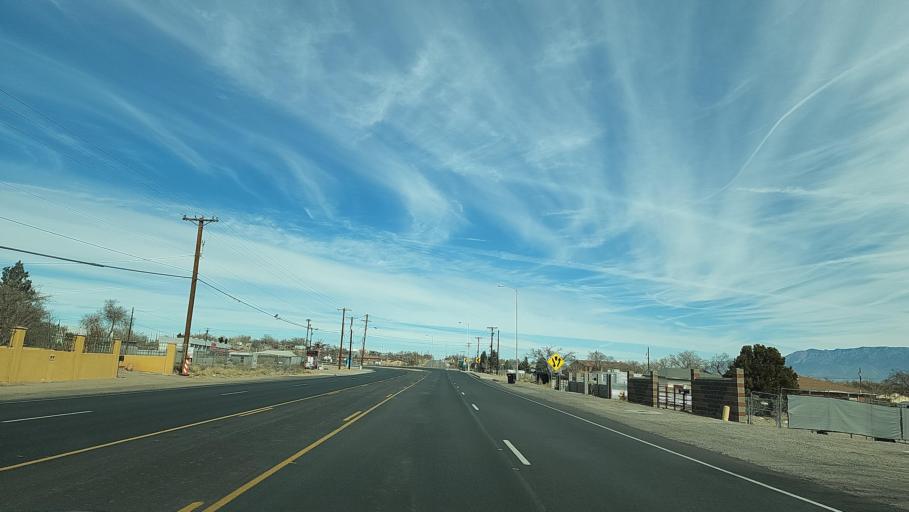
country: US
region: New Mexico
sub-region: Bernalillo County
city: South Valley
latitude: 35.0541
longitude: -106.7062
